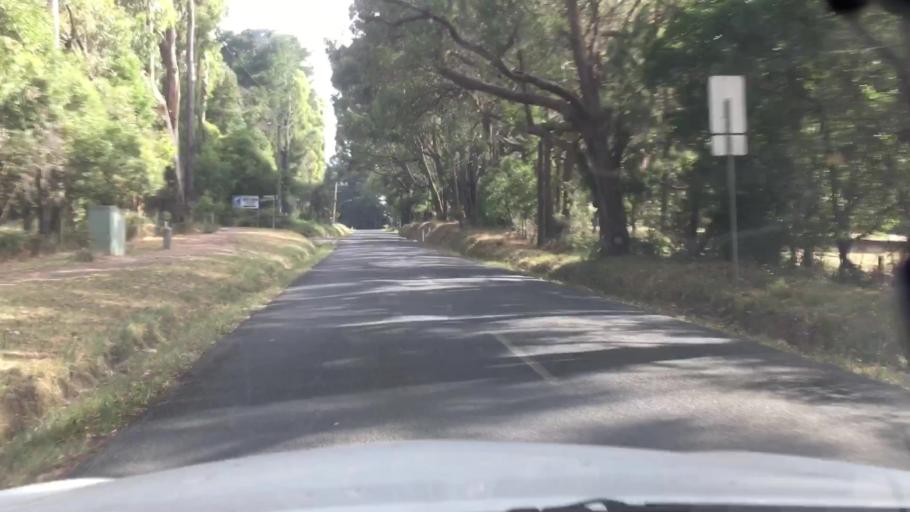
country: AU
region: Victoria
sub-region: Yarra Ranges
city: Macclesfield
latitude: -37.8876
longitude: 145.4763
